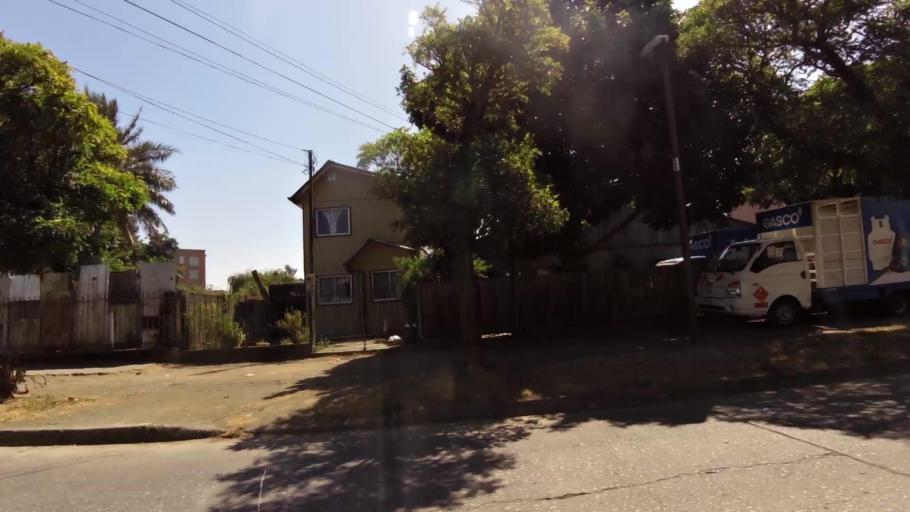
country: CL
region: Biobio
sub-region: Provincia de Concepcion
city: Concepcion
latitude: -36.8177
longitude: -73.0626
